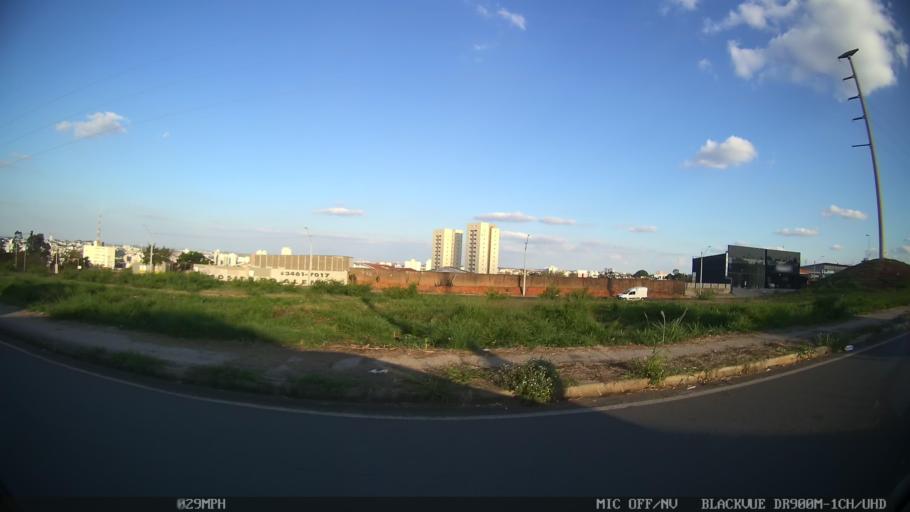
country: BR
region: Sao Paulo
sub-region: Americana
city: Americana
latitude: -22.7338
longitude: -47.3508
